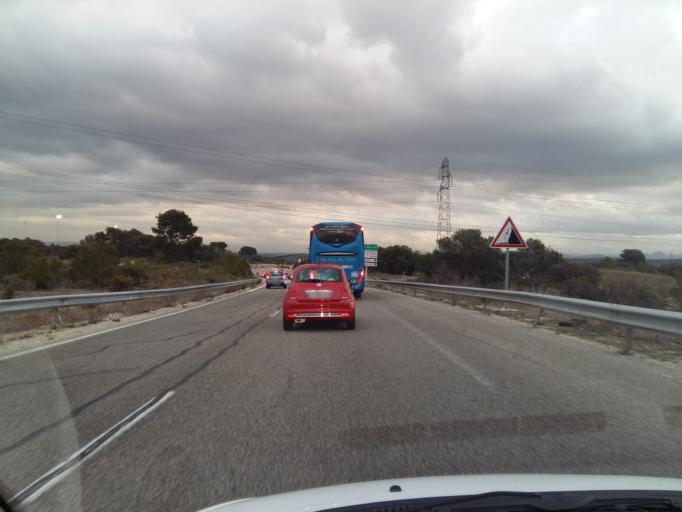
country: FR
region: Provence-Alpes-Cote d'Azur
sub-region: Departement des Bouches-du-Rhone
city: Les Pennes-Mirabeau
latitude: 43.4522
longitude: 5.3089
